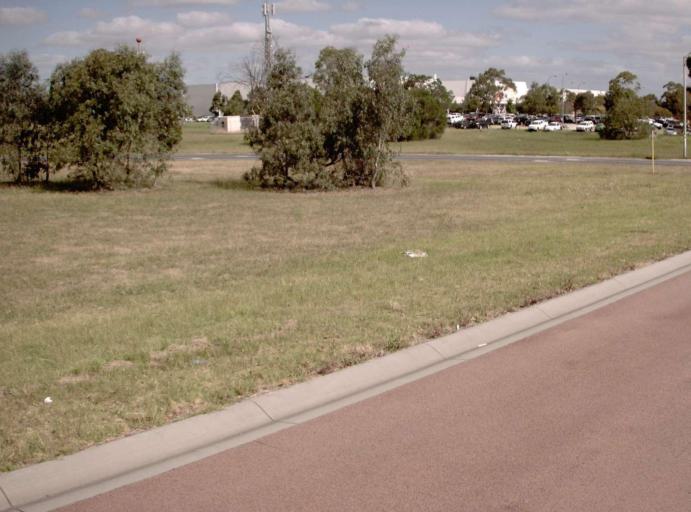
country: AU
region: Victoria
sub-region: Greater Dandenong
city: Dandenong North
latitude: -37.9618
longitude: 145.2252
